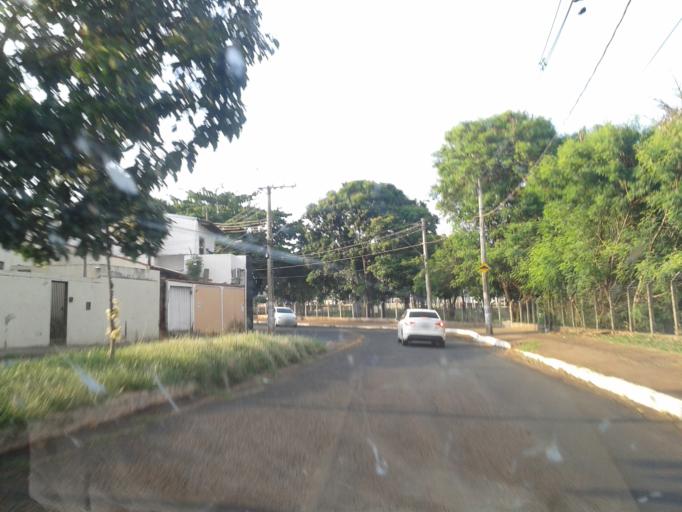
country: BR
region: Minas Gerais
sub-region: Uberlandia
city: Uberlandia
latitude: -18.9207
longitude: -48.3236
